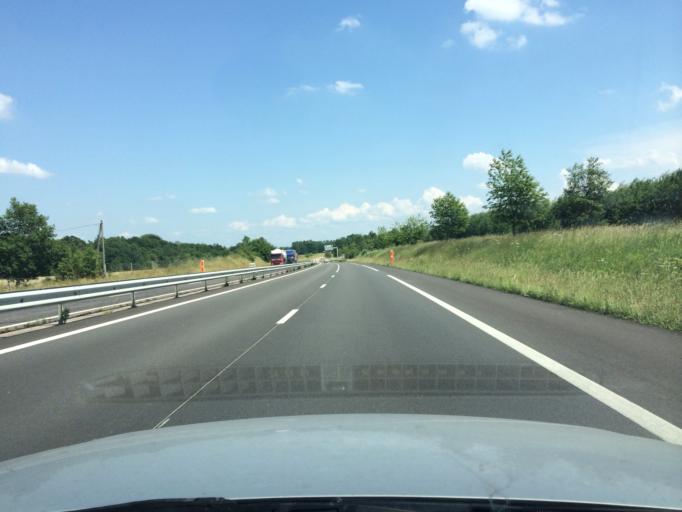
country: FR
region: Lorraine
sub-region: Departement de Meurthe-et-Moselle
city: Chanteheux
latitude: 48.5745
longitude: 6.6166
